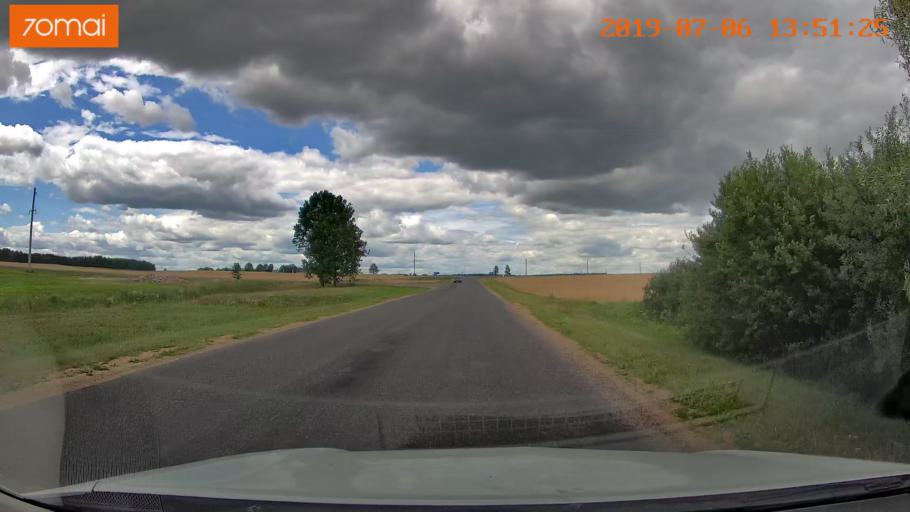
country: BY
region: Minsk
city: Ivyanyets
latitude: 53.7080
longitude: 26.8321
